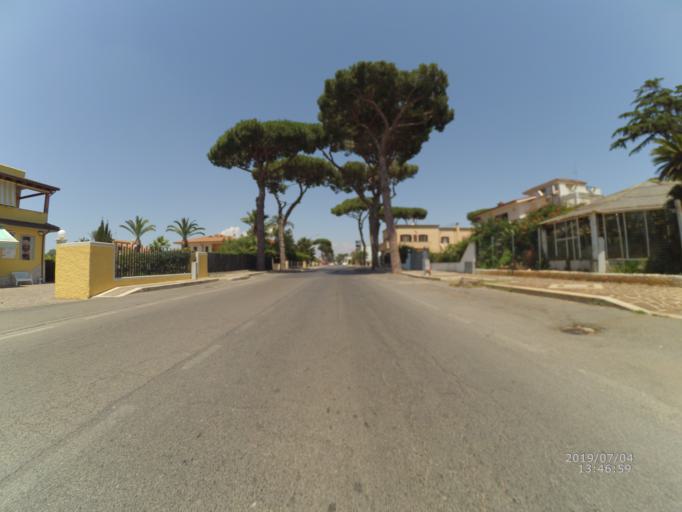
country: IT
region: Latium
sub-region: Provincia di Latina
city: San Felice Circeo
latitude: 41.2754
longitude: 13.1002
